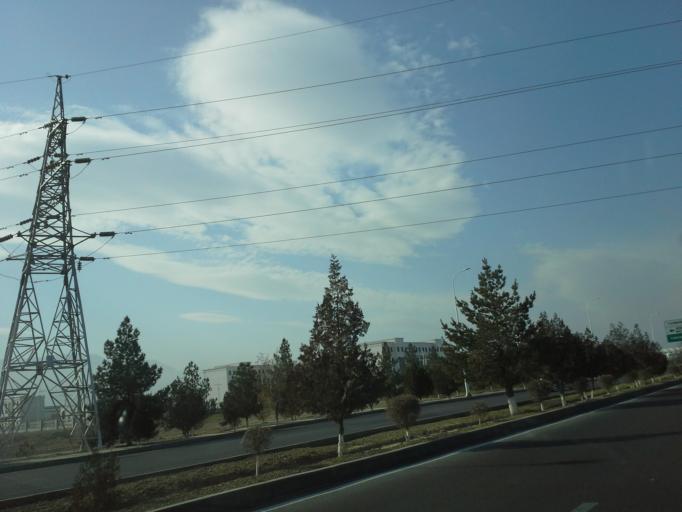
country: TM
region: Ahal
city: Abadan
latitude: 38.0422
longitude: 58.2080
